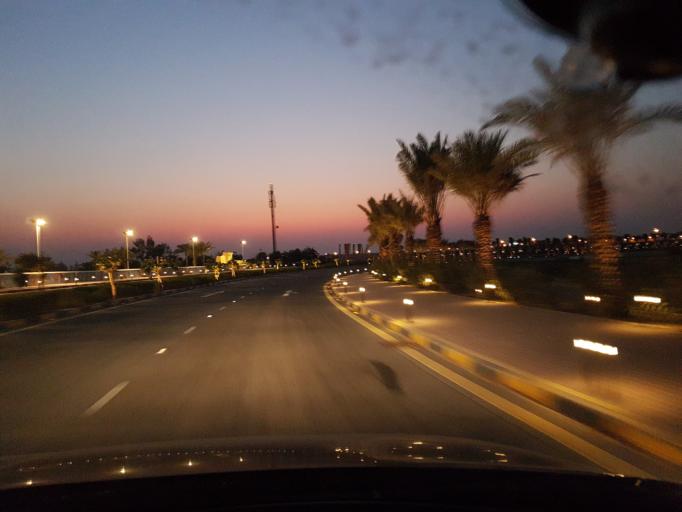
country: BH
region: Central Governorate
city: Dar Kulayb
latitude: 26.0155
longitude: 50.5107
